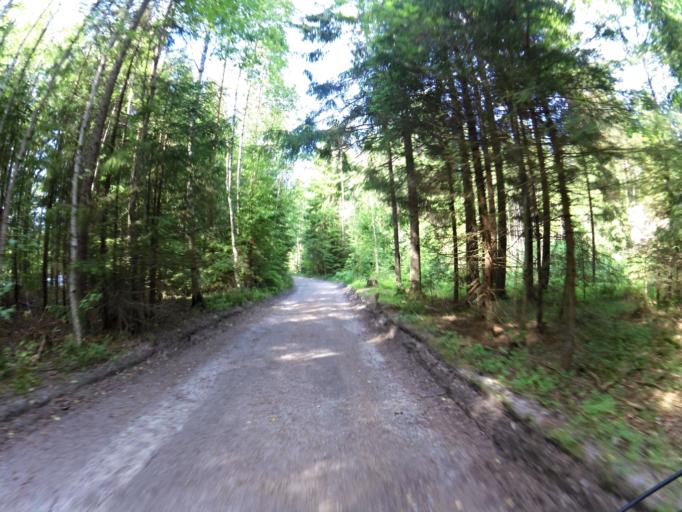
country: NO
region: Ostfold
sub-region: Fredrikstad
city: Fredrikstad
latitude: 59.2461
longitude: 10.9624
